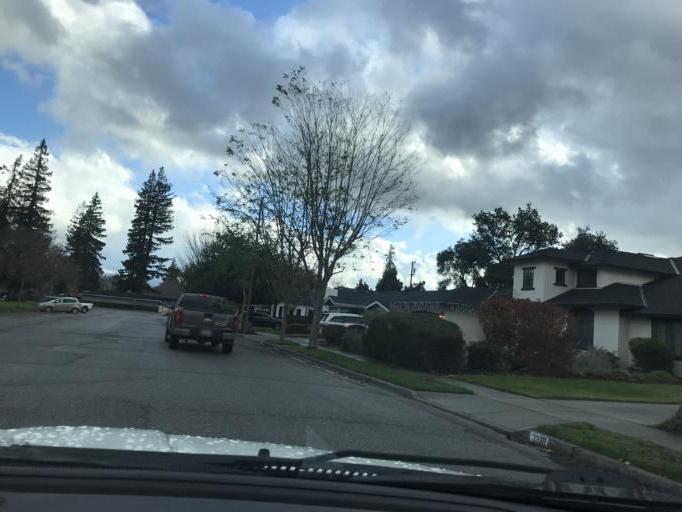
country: US
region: California
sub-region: Santa Clara County
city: Buena Vista
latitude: 37.3026
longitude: -121.9095
